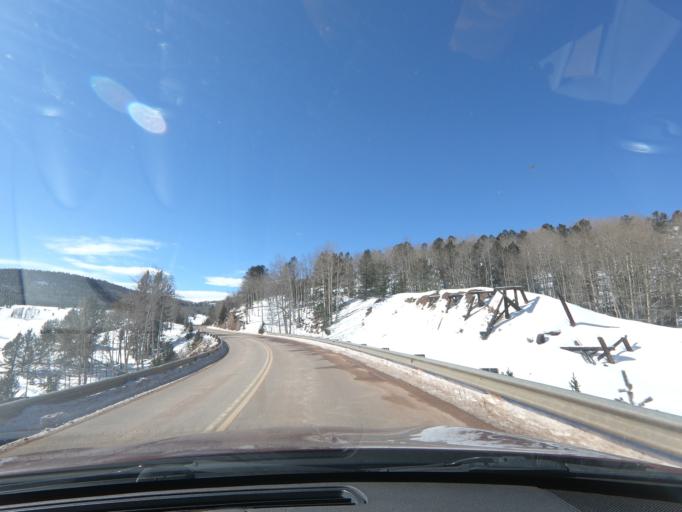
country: US
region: Colorado
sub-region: Teller County
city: Cripple Creek
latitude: 38.7432
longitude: -105.1067
